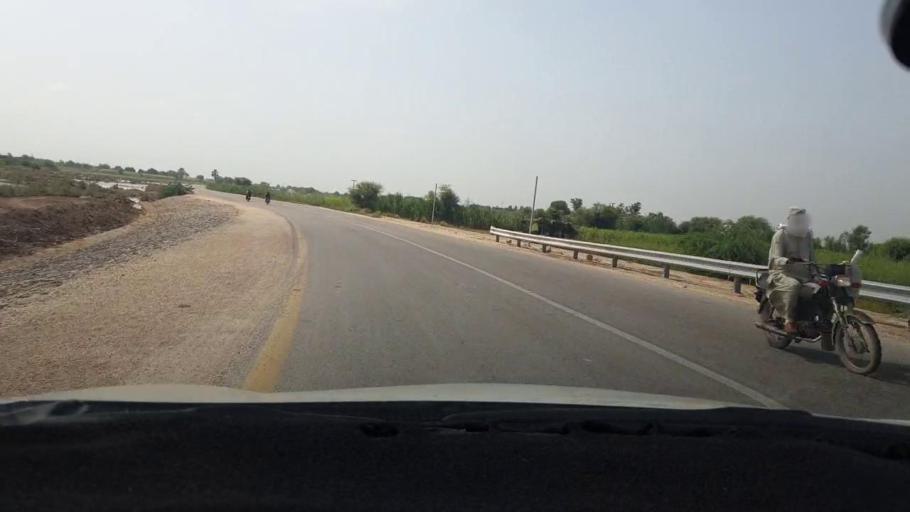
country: PK
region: Sindh
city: Mirpur Khas
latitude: 25.5906
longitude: 69.0756
